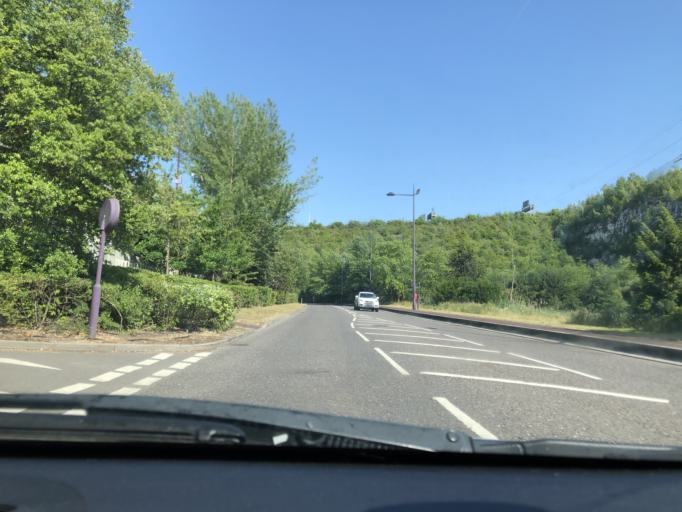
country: GB
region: England
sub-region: Kent
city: Stone
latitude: 51.4363
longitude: 0.2742
